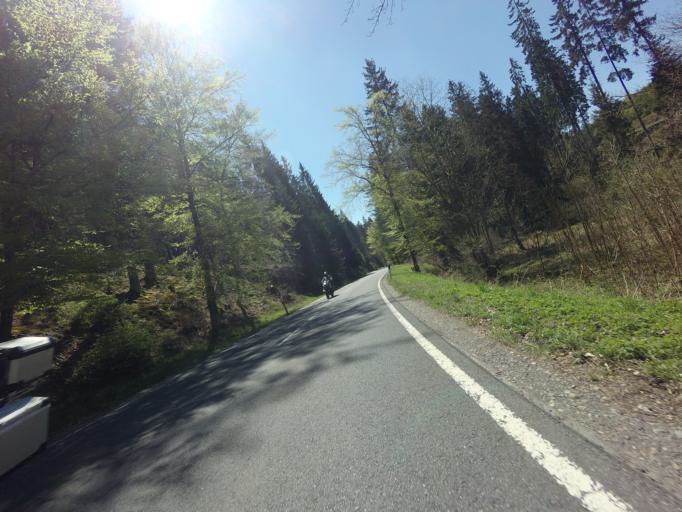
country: DE
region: North Rhine-Westphalia
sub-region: Regierungsbezirk Arnsberg
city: Erndtebruck
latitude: 51.0730
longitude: 8.2166
